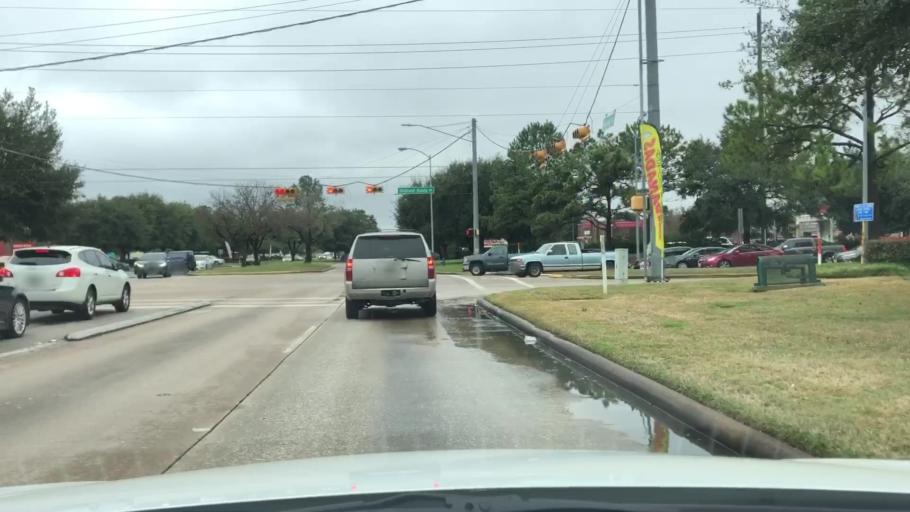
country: US
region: Texas
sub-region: Fort Bend County
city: Cinco Ranch
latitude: 29.7590
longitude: -95.7517
